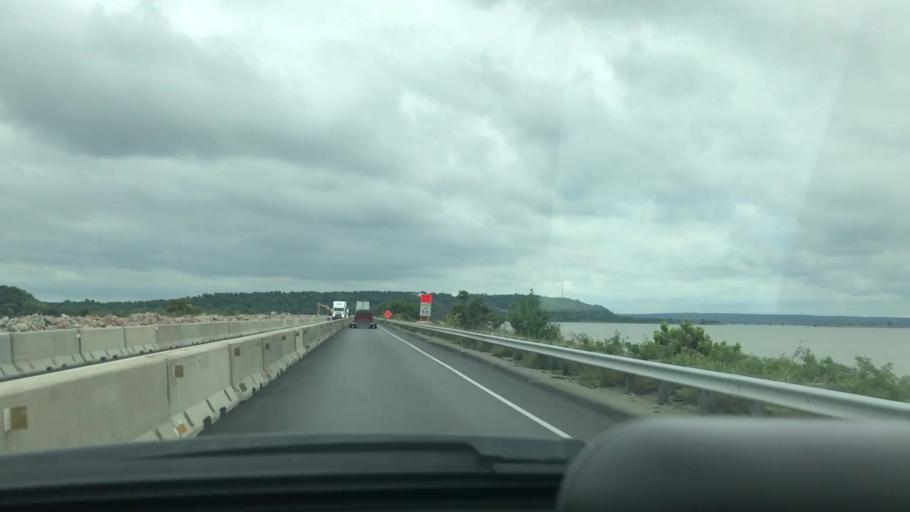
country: US
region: Oklahoma
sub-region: McIntosh County
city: Eufaula
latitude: 35.2356
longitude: -95.5924
